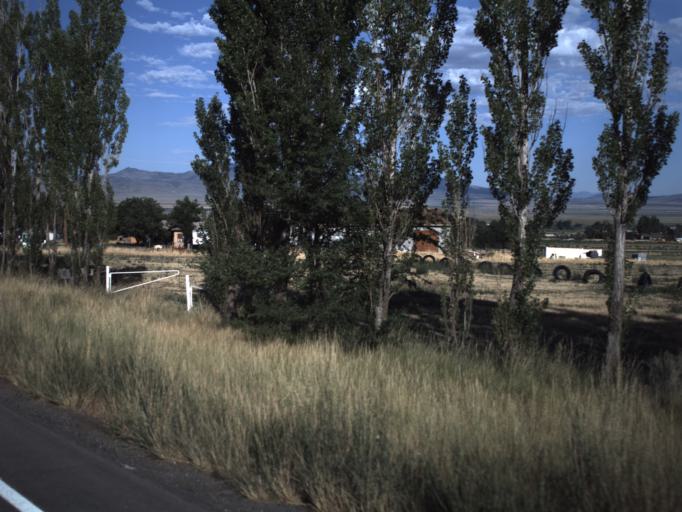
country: US
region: Utah
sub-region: Utah County
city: Genola
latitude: 39.9825
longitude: -111.8277
